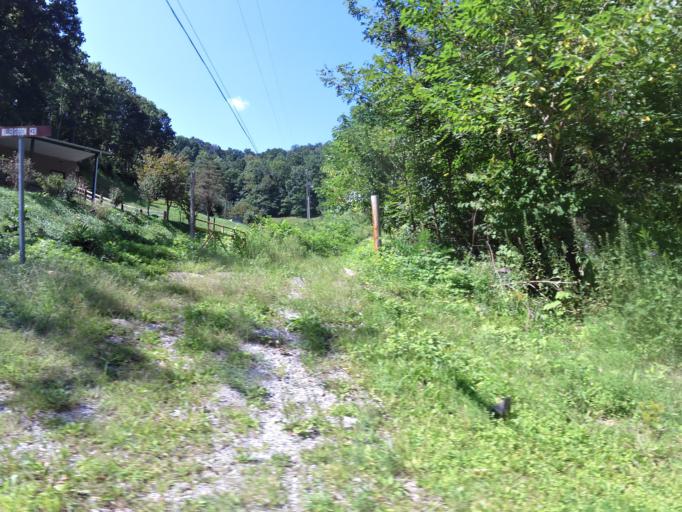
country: US
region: Kentucky
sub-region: Leslie County
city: Hyden
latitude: 37.1454
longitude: -83.4733
